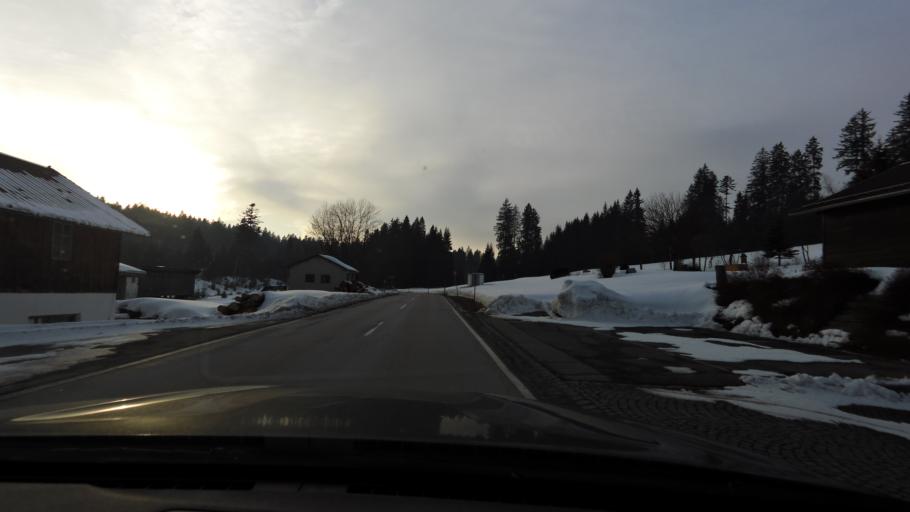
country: DE
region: Bavaria
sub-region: Lower Bavaria
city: Philippsreut
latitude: 48.8648
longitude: 13.7134
